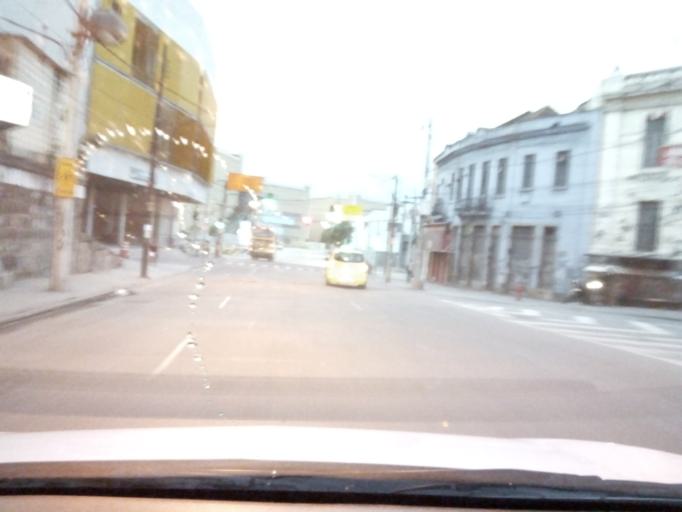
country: BR
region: Rio de Janeiro
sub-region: Rio De Janeiro
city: Rio de Janeiro
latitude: -22.8978
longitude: -43.1955
